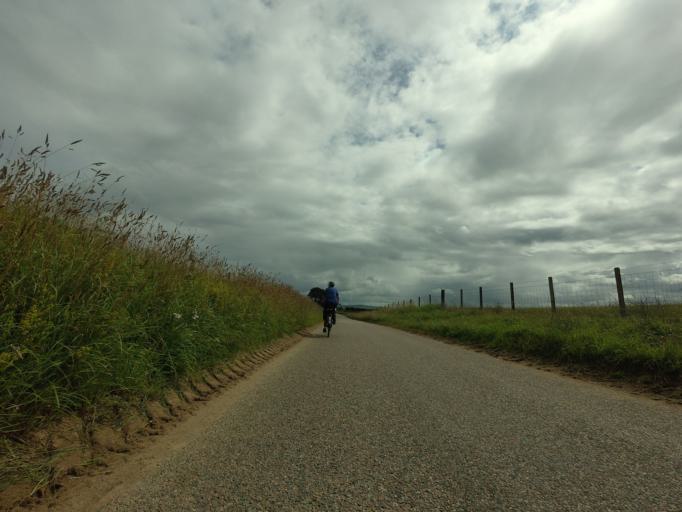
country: GB
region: Scotland
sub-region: Moray
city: Fochabers
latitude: 57.6669
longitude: -3.1469
